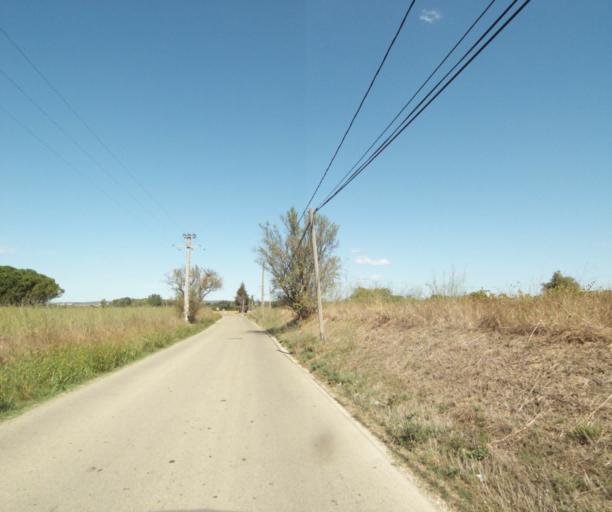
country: FR
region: Languedoc-Roussillon
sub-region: Departement du Gard
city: Bouillargues
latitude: 43.8117
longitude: 4.4177
